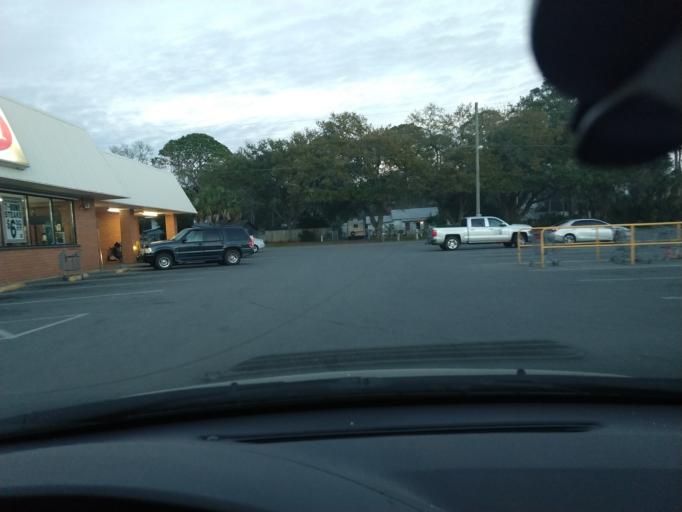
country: US
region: Florida
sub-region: Franklin County
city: Apalachicola
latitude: 29.7150
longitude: -85.0057
